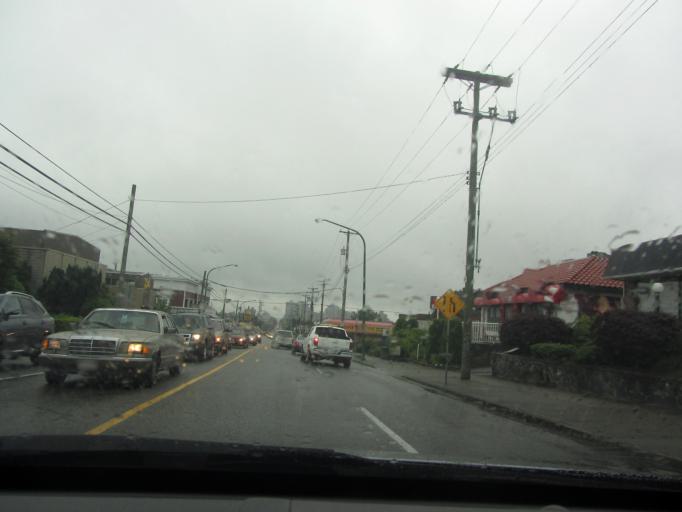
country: CA
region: British Columbia
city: New Westminster
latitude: 49.2238
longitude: -122.9337
